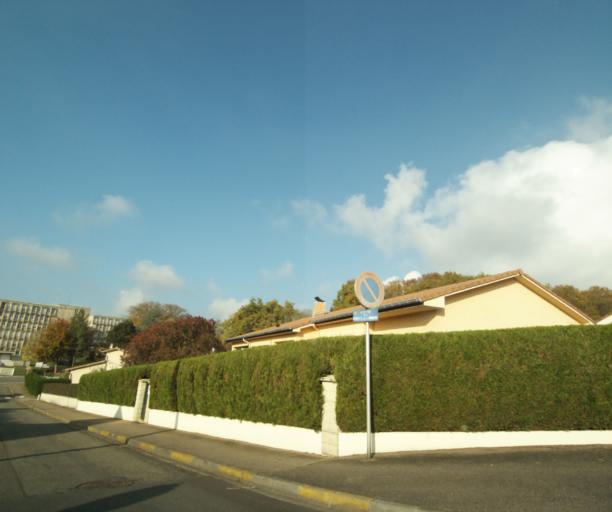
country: FR
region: Lorraine
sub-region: Departement de Meurthe-et-Moselle
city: Briey
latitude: 49.2574
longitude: 5.9364
